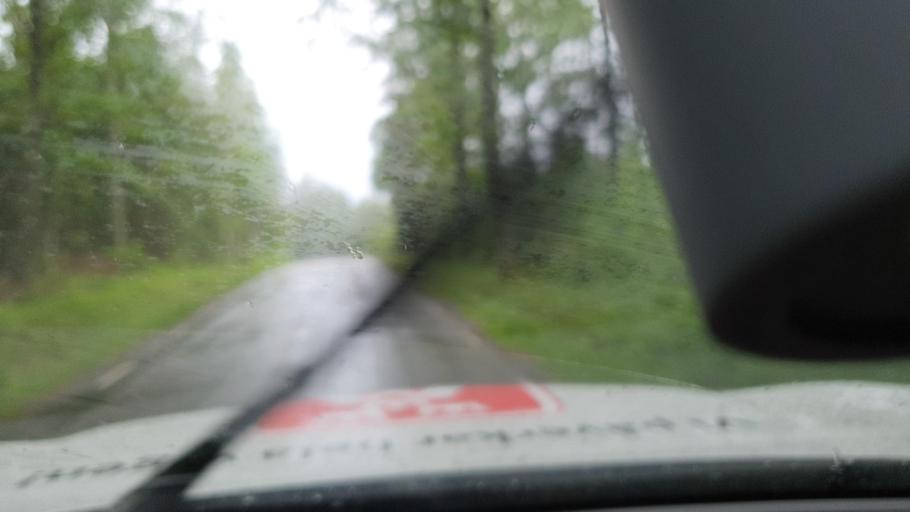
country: SE
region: Vaestra Goetaland
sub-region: Mariestads Kommun
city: Mariestad
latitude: 58.7710
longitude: 13.9455
